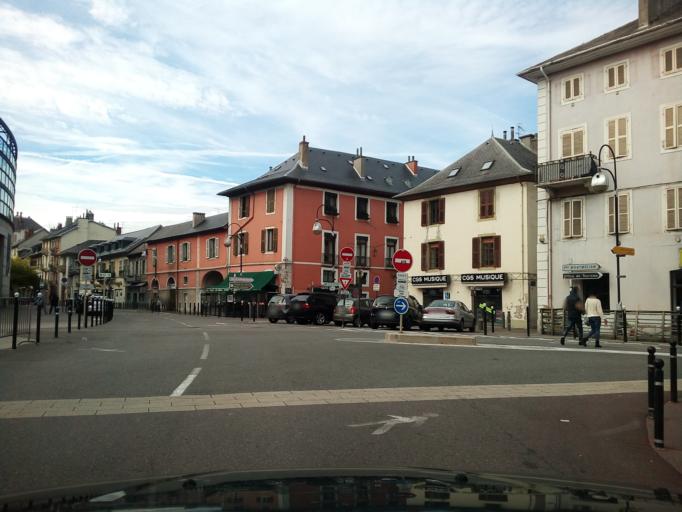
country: FR
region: Rhone-Alpes
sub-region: Departement de la Savoie
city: Chambery
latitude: 45.5641
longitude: 5.9253
